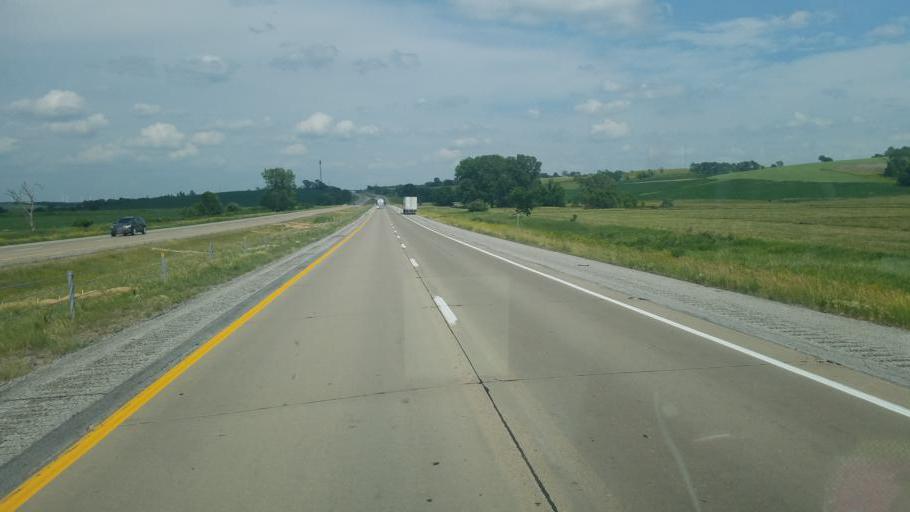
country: US
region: Iowa
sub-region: Cass County
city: Atlantic
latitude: 41.4962
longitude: -94.7929
